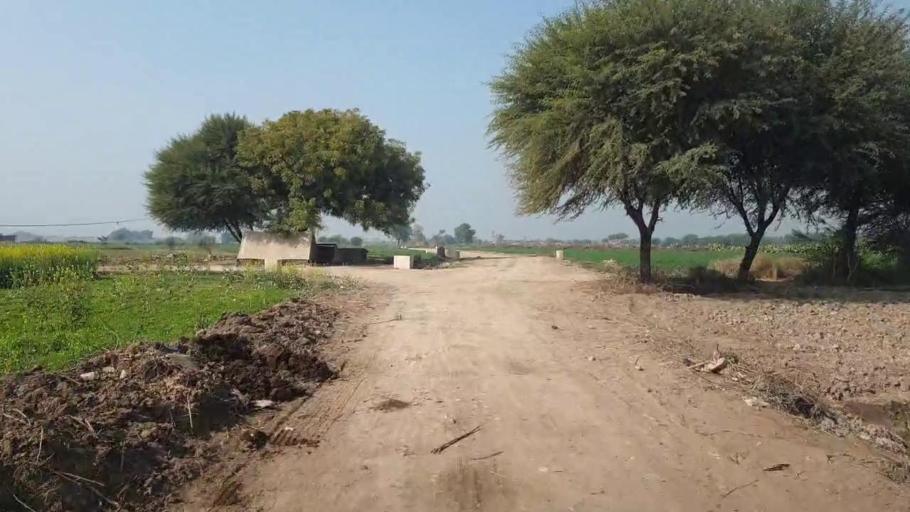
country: PK
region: Sindh
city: Bhit Shah
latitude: 25.7245
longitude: 68.5014
